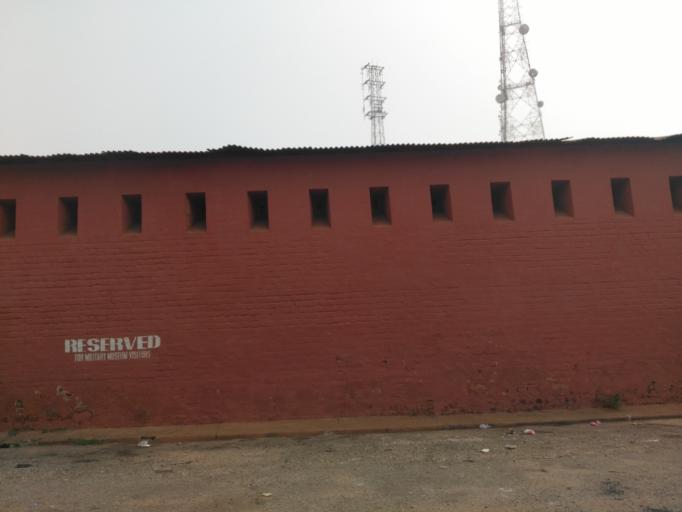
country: GH
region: Ashanti
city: Kumasi
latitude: 6.6911
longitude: -1.6250
